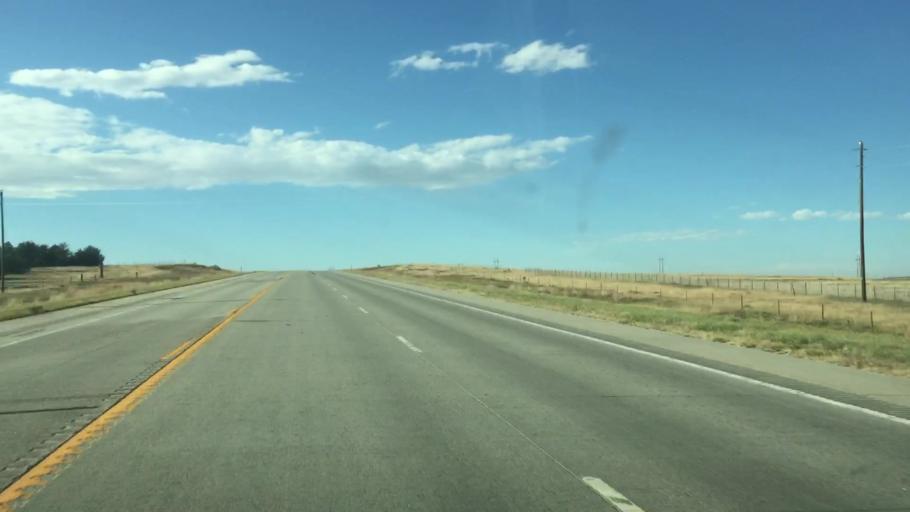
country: US
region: Colorado
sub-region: Lincoln County
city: Limon
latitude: 39.2423
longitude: -103.6269
